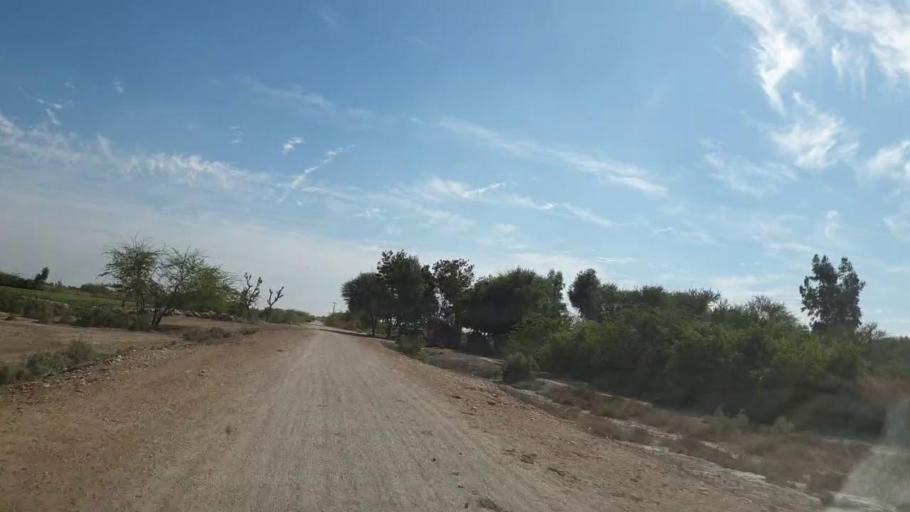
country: PK
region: Sindh
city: Pithoro
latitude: 25.5682
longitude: 69.3007
